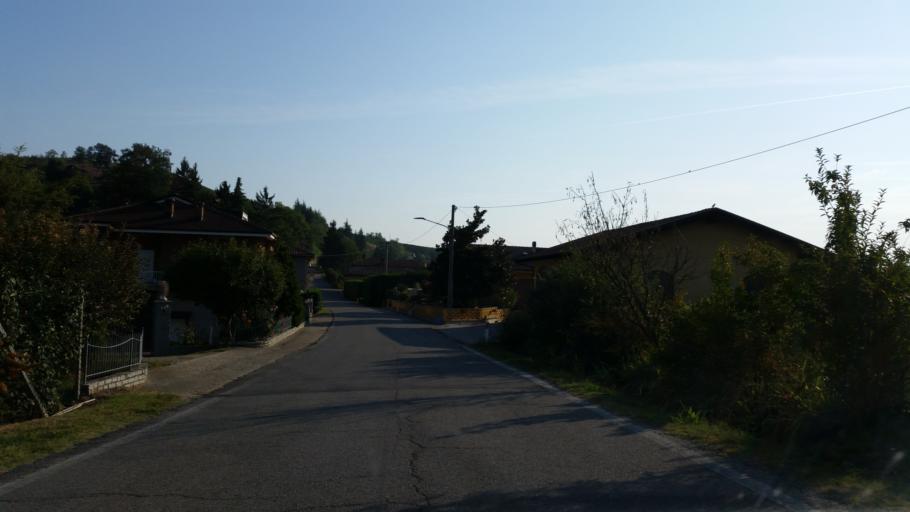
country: IT
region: Piedmont
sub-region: Provincia di Cuneo
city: Mango
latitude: 44.6926
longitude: 8.1510
